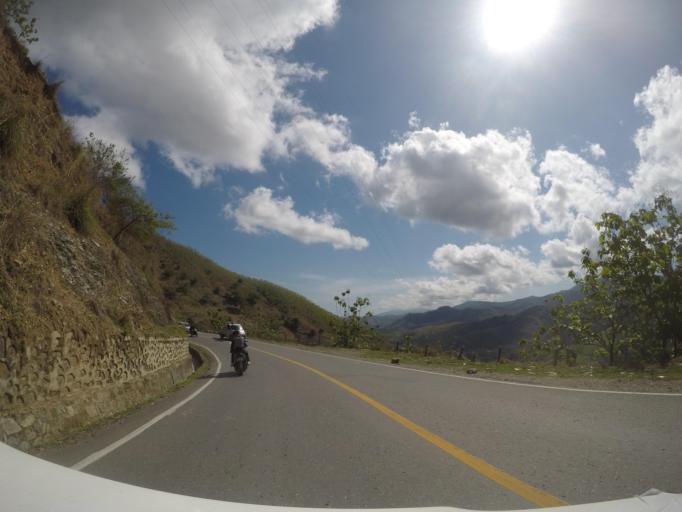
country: TL
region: Dili
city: Dili
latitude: -8.5626
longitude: 125.6342
